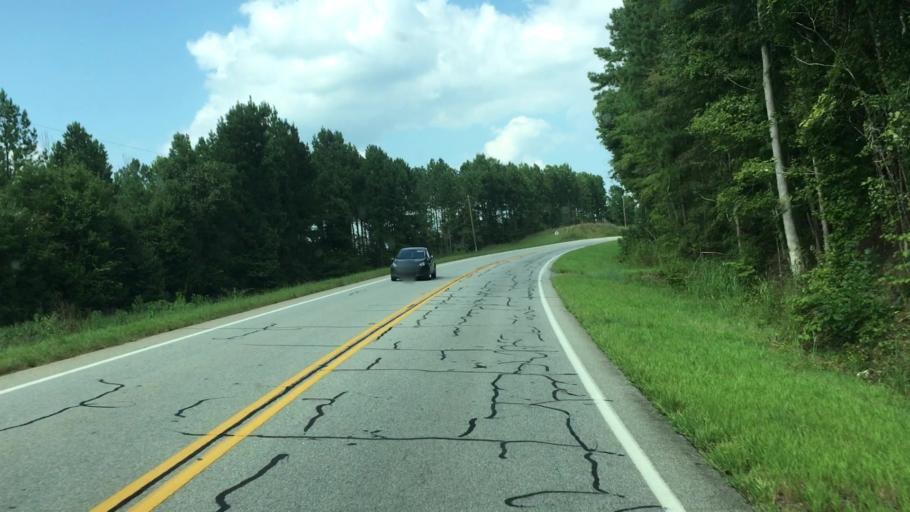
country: US
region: Georgia
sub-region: Butts County
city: Indian Springs
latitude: 33.1829
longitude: -83.7905
